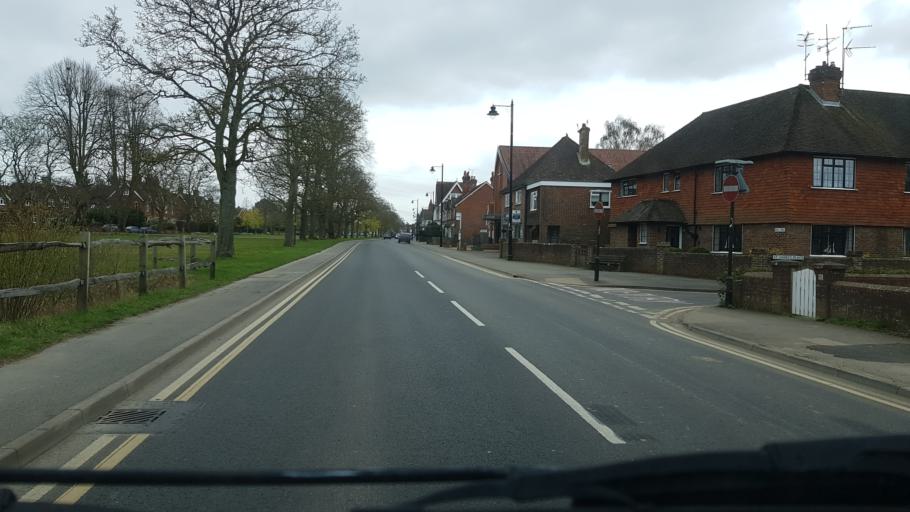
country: GB
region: England
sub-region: Surrey
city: Cranleigh
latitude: 51.1434
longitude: -0.4962
